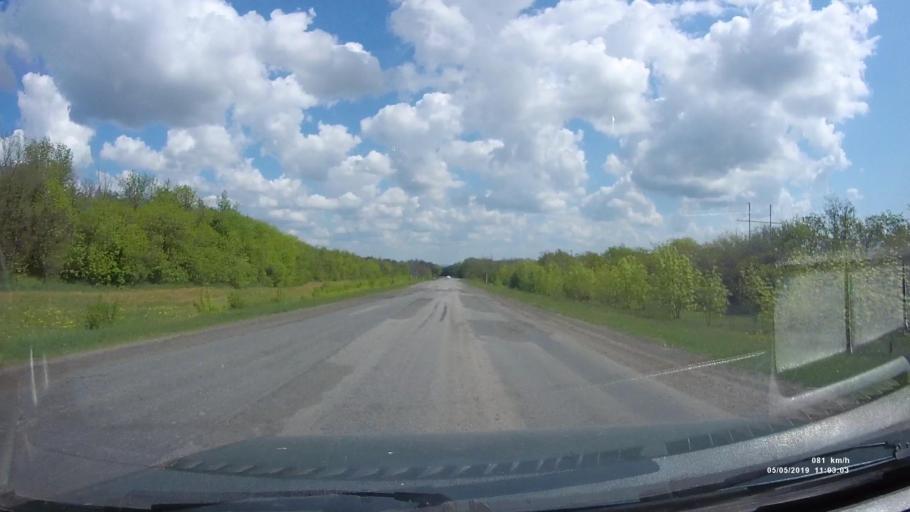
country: RU
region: Rostov
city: Ust'-Donetskiy
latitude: 47.6888
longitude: 40.9157
